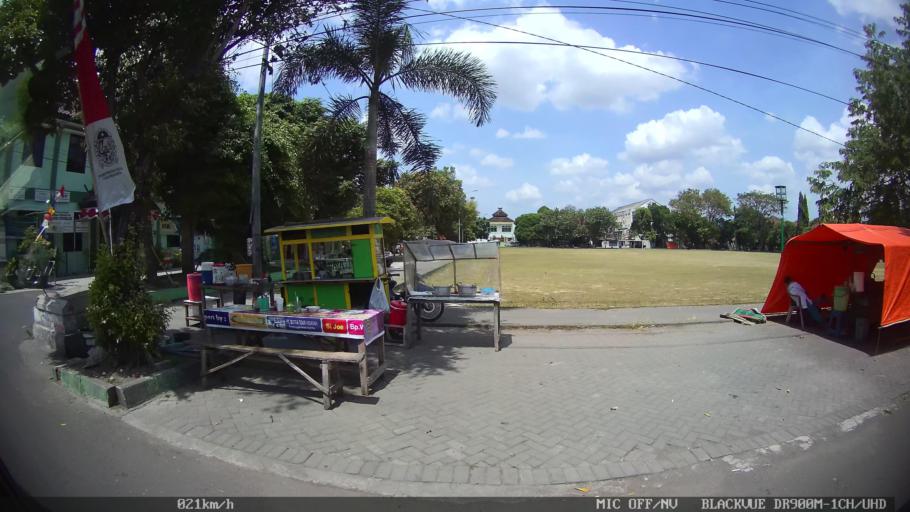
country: ID
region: Daerah Istimewa Yogyakarta
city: Yogyakarta
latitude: -7.8047
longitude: 110.3529
